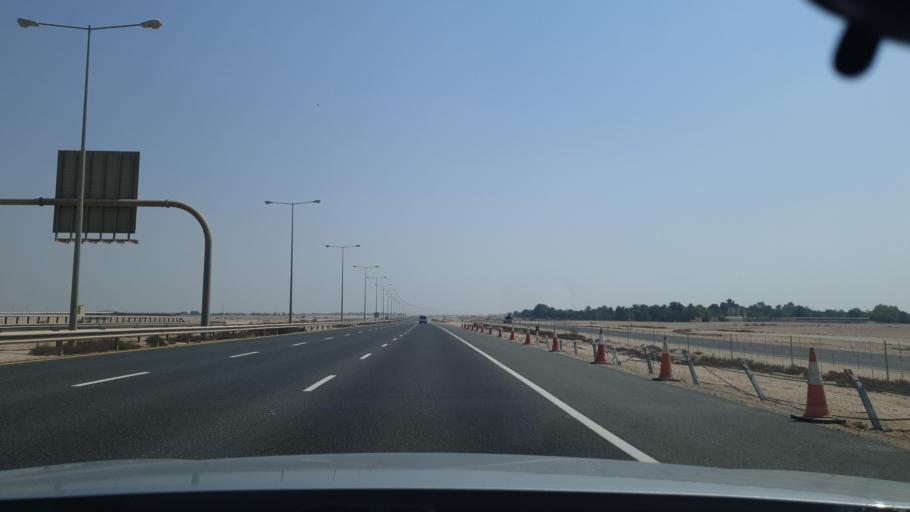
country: QA
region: Al Khawr
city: Al Khawr
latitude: 25.7831
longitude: 51.3997
